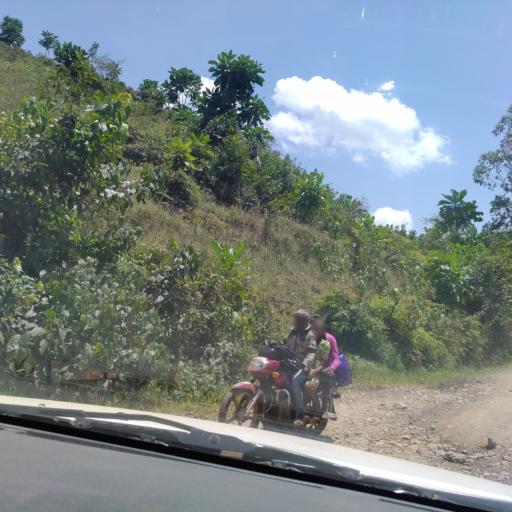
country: CD
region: Nord Kivu
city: Sake
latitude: -1.9676
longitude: 28.9149
